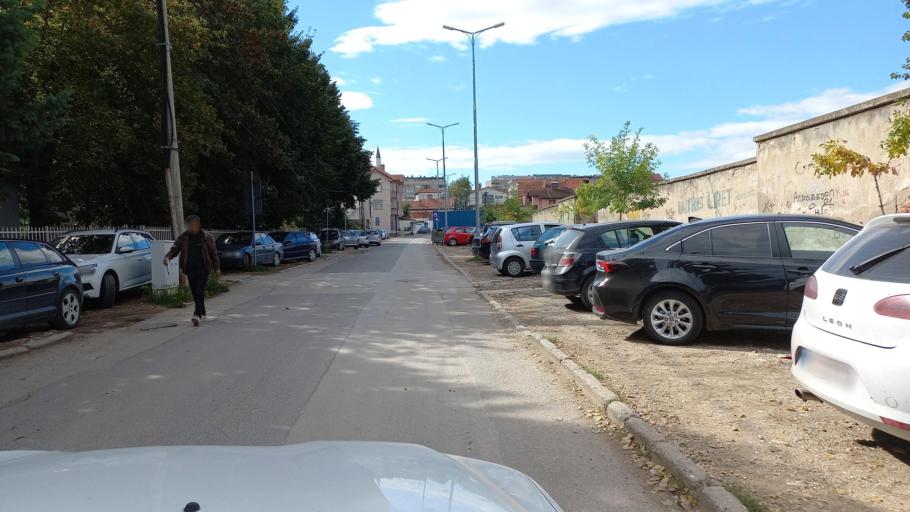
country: MK
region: Kumanovo
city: Kumanovo
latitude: 42.1397
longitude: 21.7153
